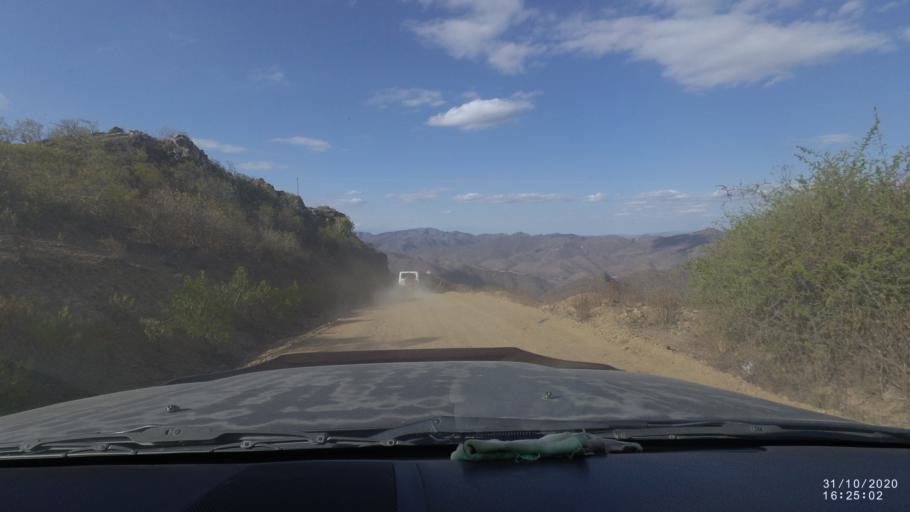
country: BO
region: Chuquisaca
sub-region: Provincia Zudanez
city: Mojocoya
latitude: -18.4035
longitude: -64.5881
